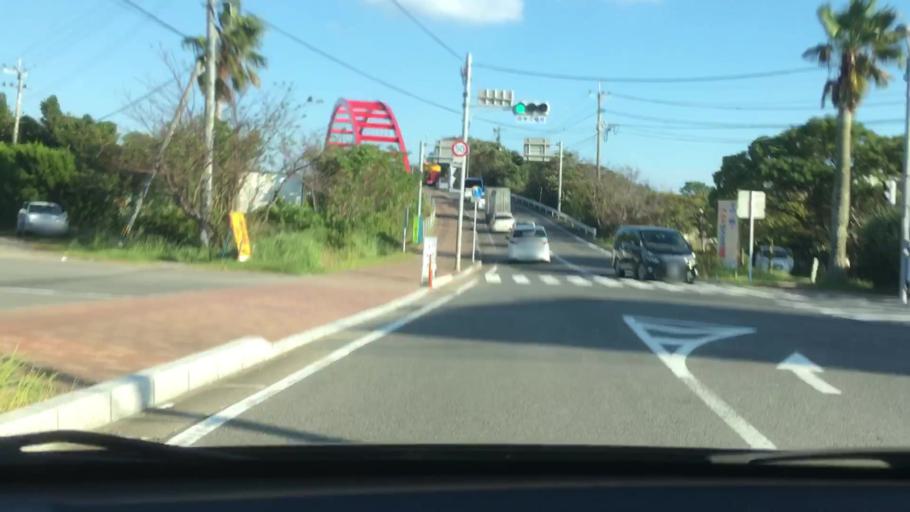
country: JP
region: Nagasaki
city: Sasebo
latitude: 33.0381
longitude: 129.6255
